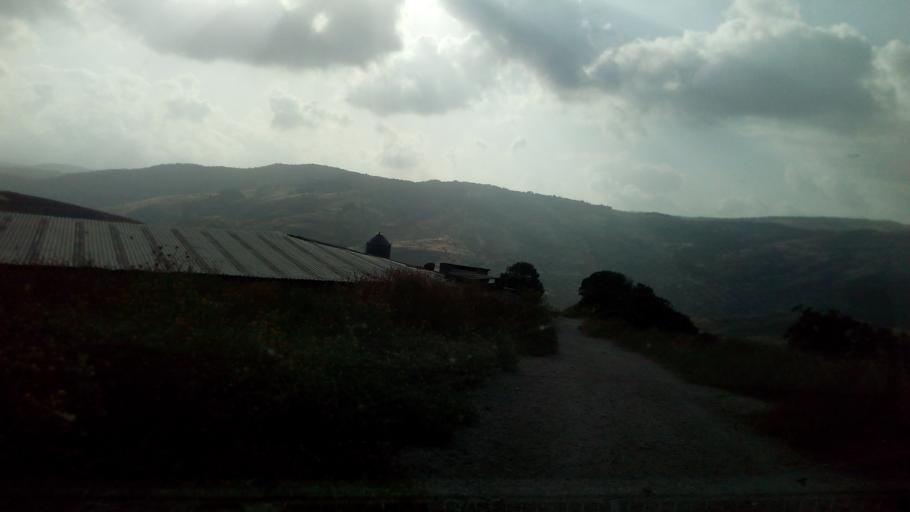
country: CY
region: Limassol
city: Pachna
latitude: 34.8192
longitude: 32.6430
